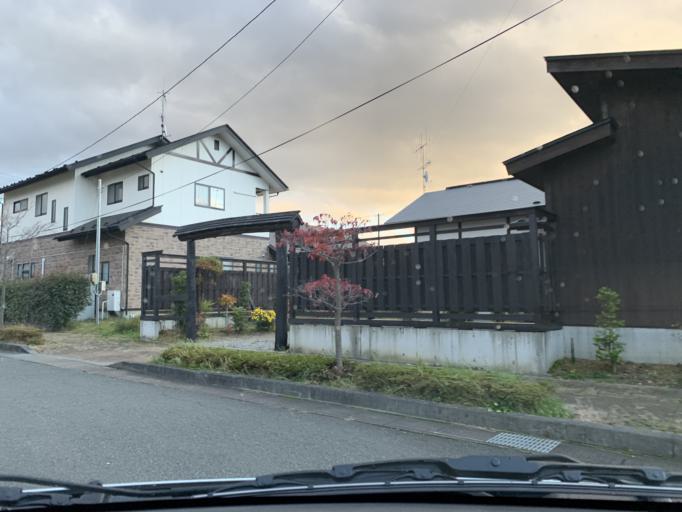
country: JP
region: Iwate
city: Mizusawa
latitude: 39.0494
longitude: 141.1267
